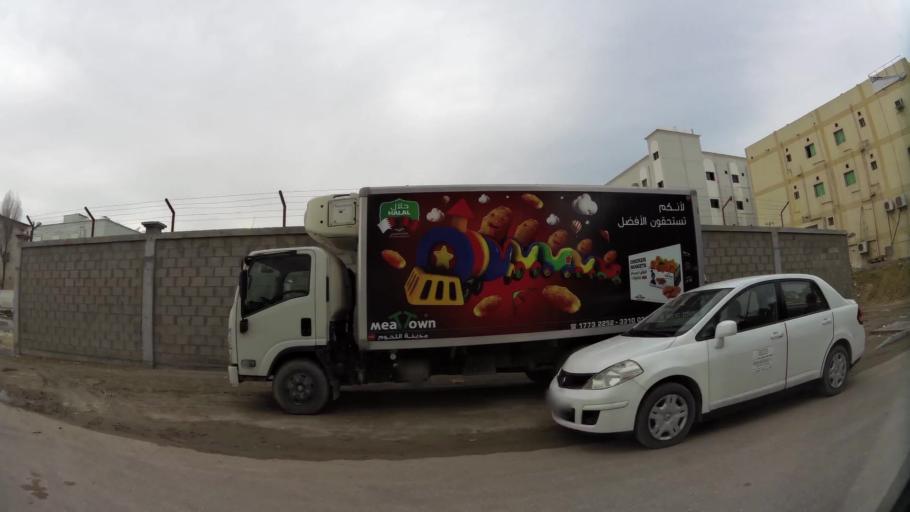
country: BH
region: Northern
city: Sitrah
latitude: 26.1721
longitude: 50.6039
